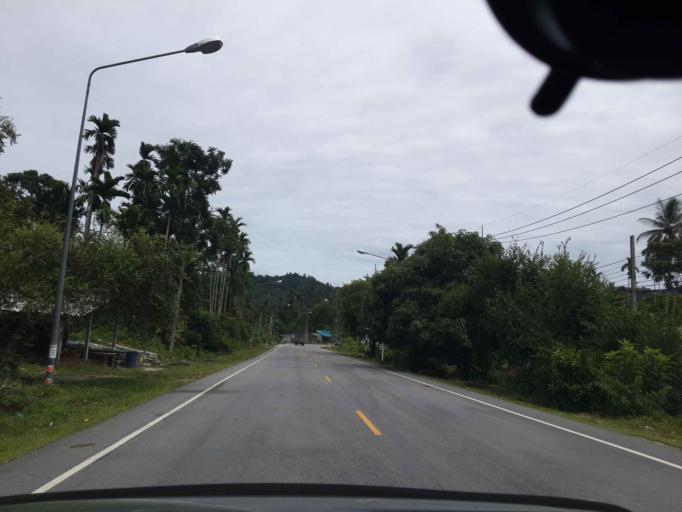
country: TH
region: Narathiwat
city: Rueso
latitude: 6.3660
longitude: 101.5934
